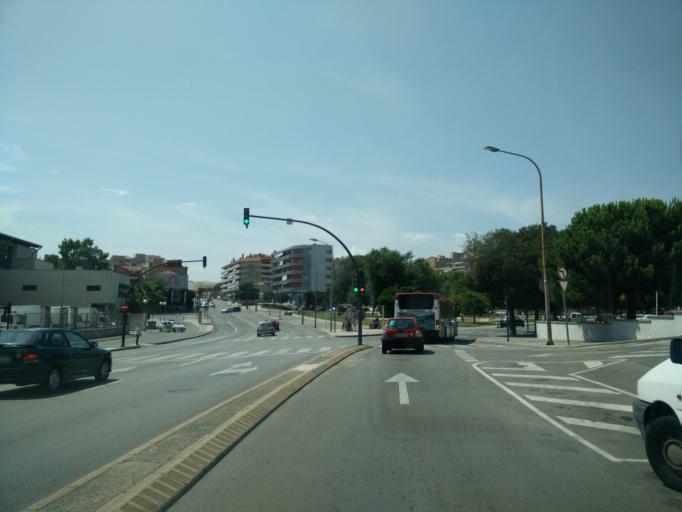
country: ES
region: Catalonia
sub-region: Provincia de Barcelona
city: Terrassa
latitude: 41.5586
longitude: 2.0297
